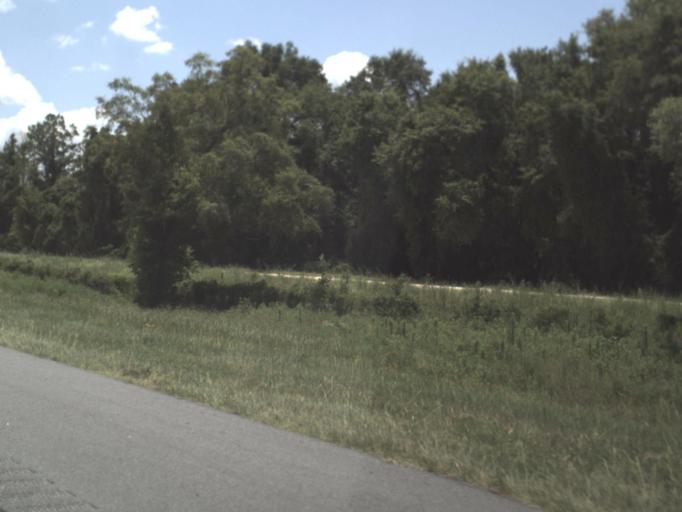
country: US
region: Florida
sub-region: Madison County
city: Madison
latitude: 30.3821
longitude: -83.3076
